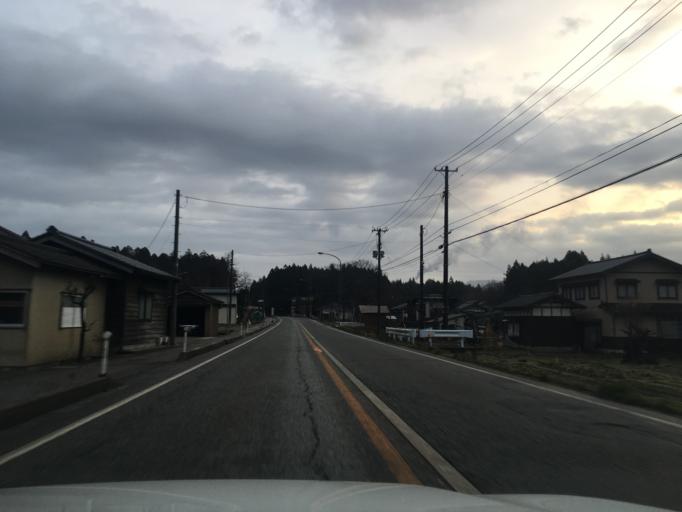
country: JP
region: Niigata
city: Murakami
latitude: 38.2962
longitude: 139.5332
